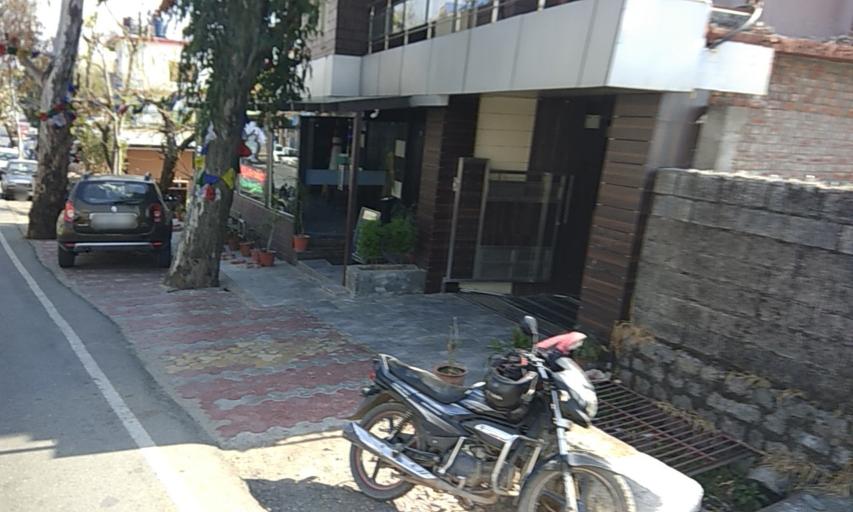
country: IN
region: Himachal Pradesh
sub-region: Kangra
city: Dharmsala
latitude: 32.1855
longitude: 76.3669
